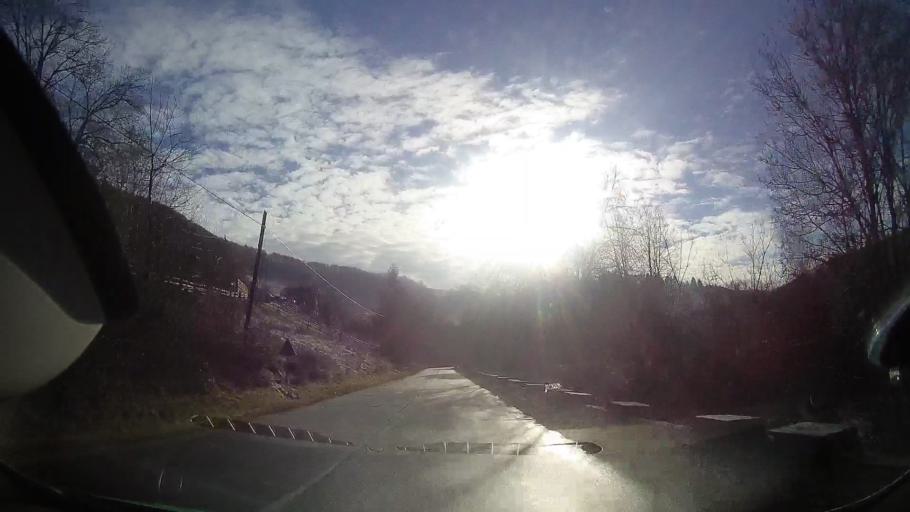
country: RO
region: Alba
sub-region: Comuna Sohodol
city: Sohodol
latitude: 46.3687
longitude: 23.0275
